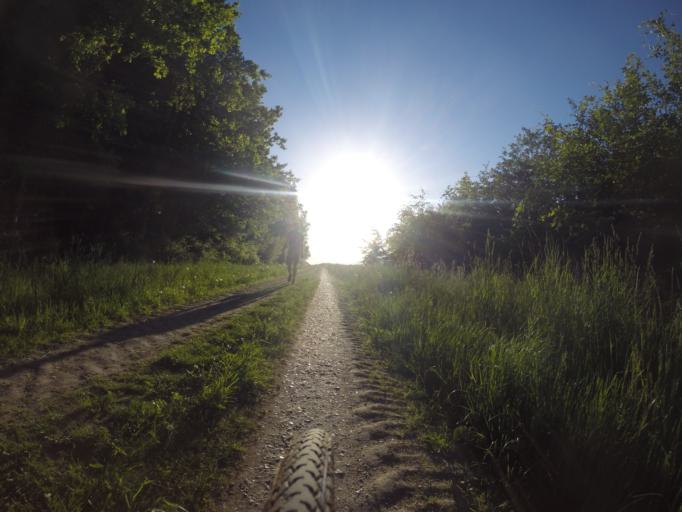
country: DK
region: Capital Region
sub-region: Hoje-Taastrup Kommune
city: Taastrup
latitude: 55.6867
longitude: 12.3070
